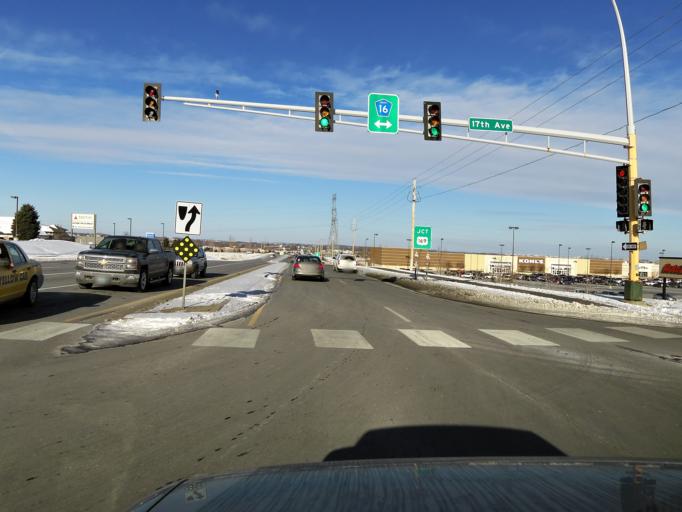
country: US
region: Minnesota
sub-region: Scott County
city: Shakopee
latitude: 44.7739
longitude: -93.5053
